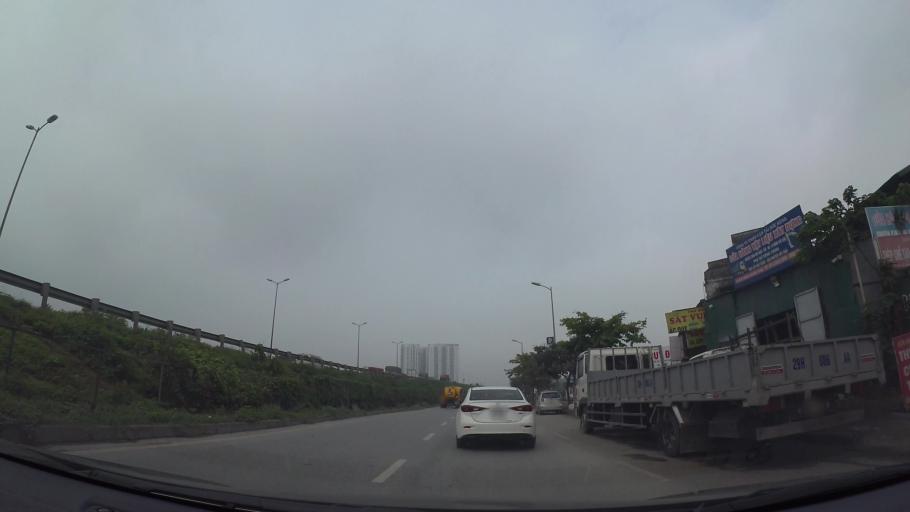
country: VN
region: Ha Noi
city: Van Dien
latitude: 20.9646
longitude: 105.8714
